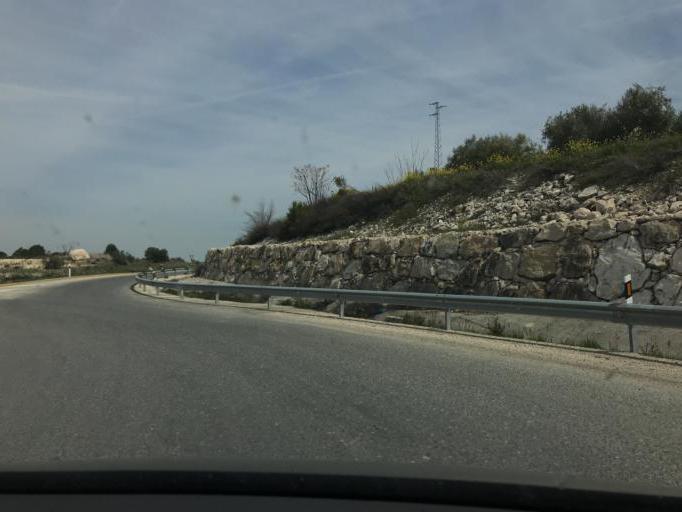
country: ES
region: Andalusia
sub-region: Provincia de Jaen
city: Jamilena
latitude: 37.7607
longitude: -3.9200
